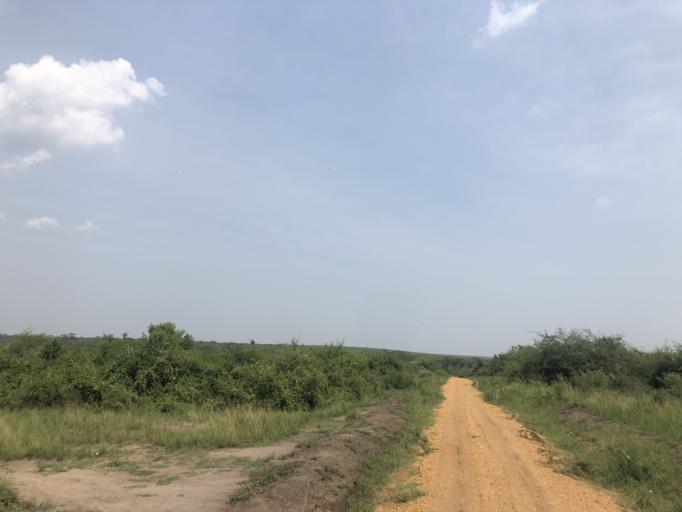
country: UG
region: Western Region
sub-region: Rubirizi District
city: Rubirizi
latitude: -0.2124
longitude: 29.9524
